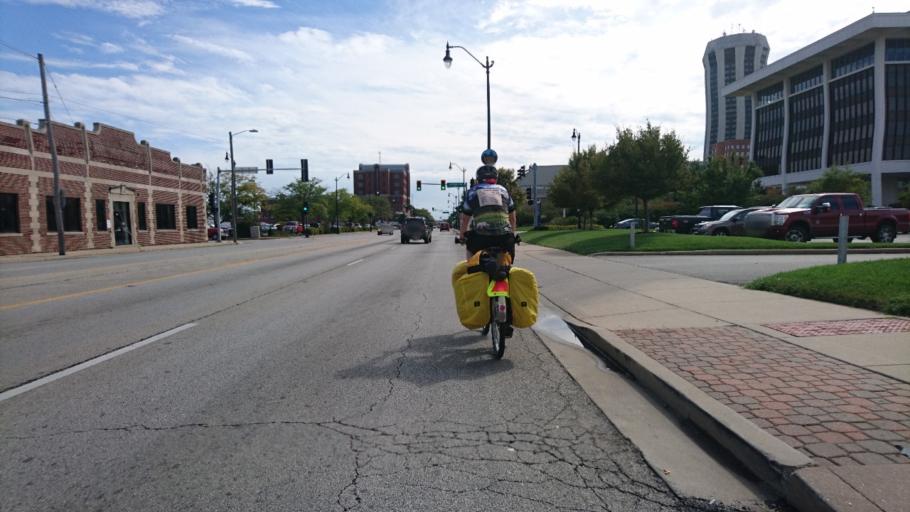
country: US
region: Illinois
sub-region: Sangamon County
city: Springfield
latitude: 39.8034
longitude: -89.6437
